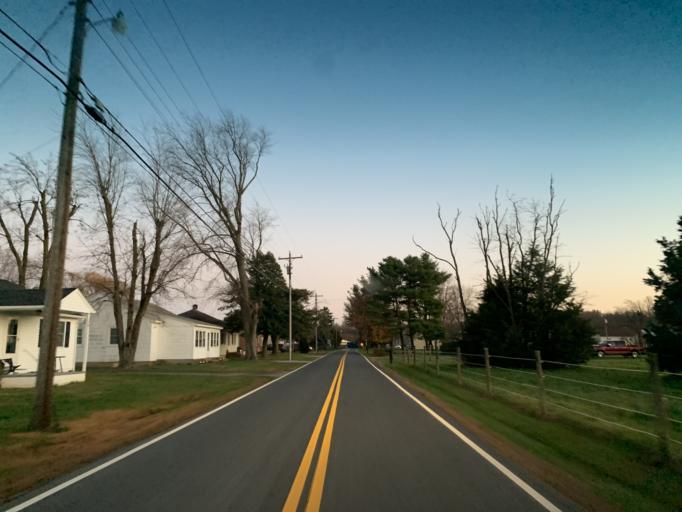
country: US
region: Delaware
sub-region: New Castle County
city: Middletown
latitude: 39.4181
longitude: -75.7798
